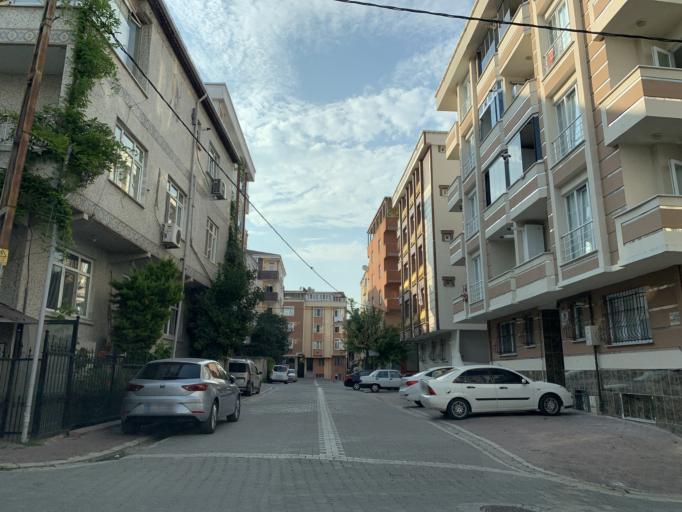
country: TR
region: Istanbul
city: Esenyurt
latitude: 41.0406
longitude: 28.6818
